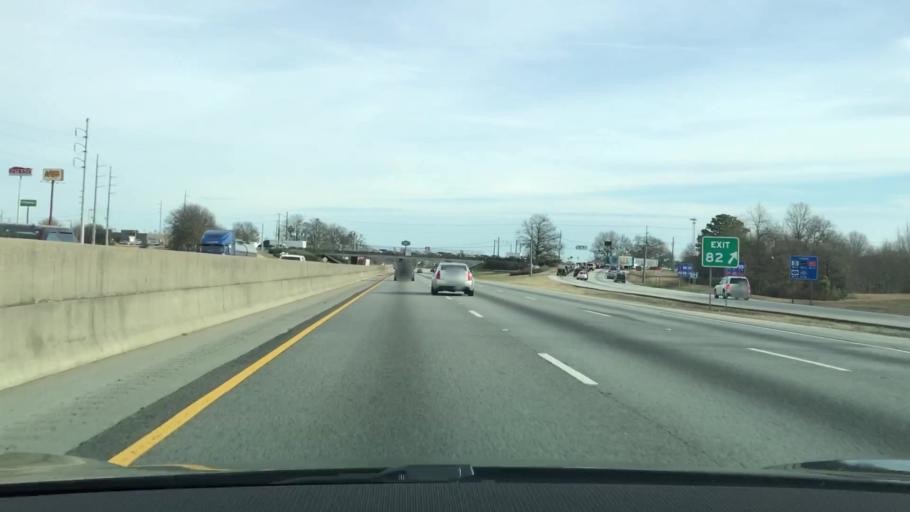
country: US
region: Georgia
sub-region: Rockdale County
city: Conyers
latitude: 33.6546
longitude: -84.0090
